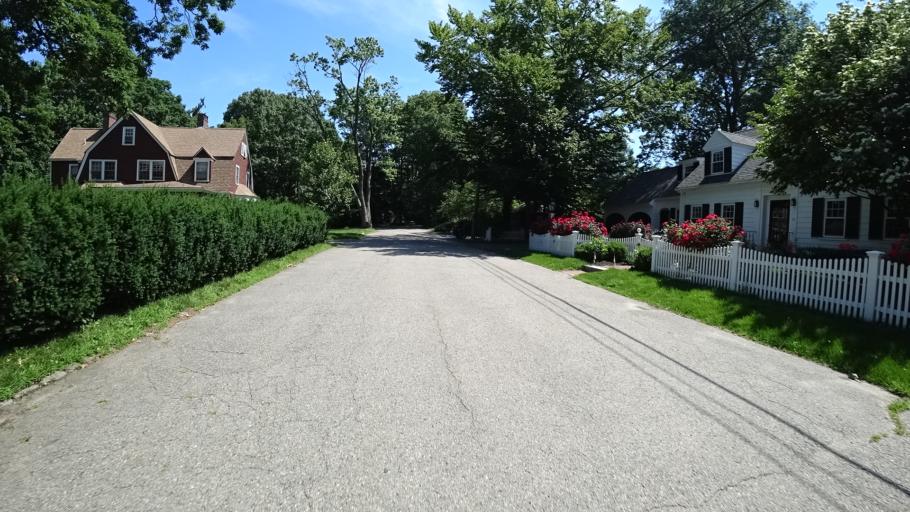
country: US
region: Massachusetts
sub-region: Norfolk County
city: Dedham
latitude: 42.2434
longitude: -71.1608
